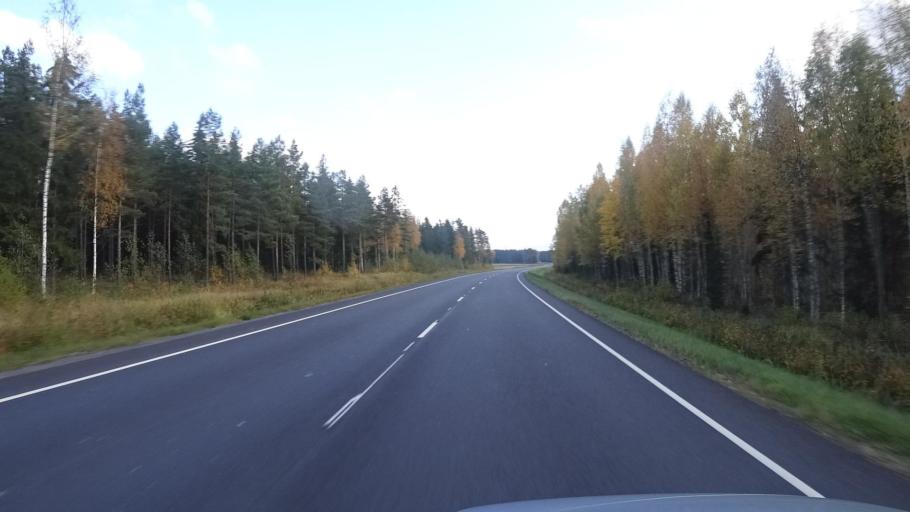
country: FI
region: Satakunta
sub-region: Rauma
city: Koeylioe
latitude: 61.1012
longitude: 22.2343
